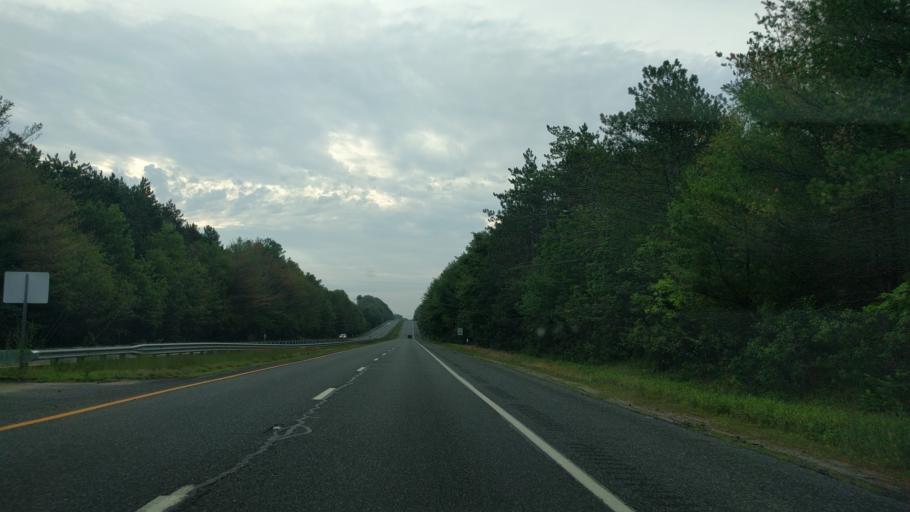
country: US
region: Massachusetts
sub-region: Worcester County
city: Millville
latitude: 42.0118
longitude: -71.5823
